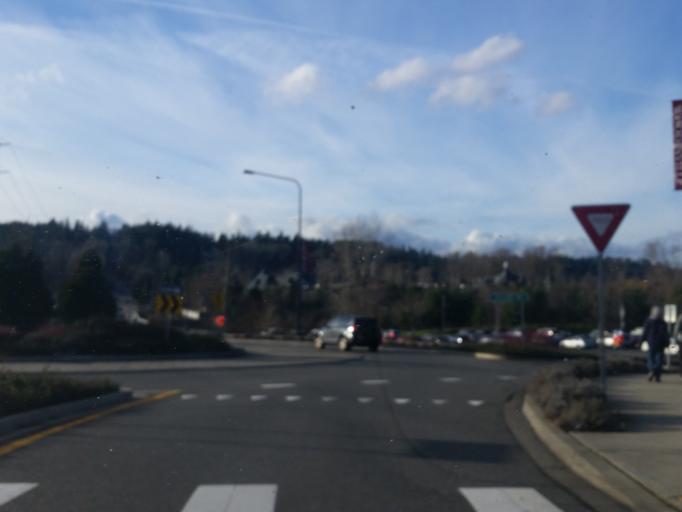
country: US
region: Washington
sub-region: King County
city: Woodinville
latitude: 47.7328
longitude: -122.1435
